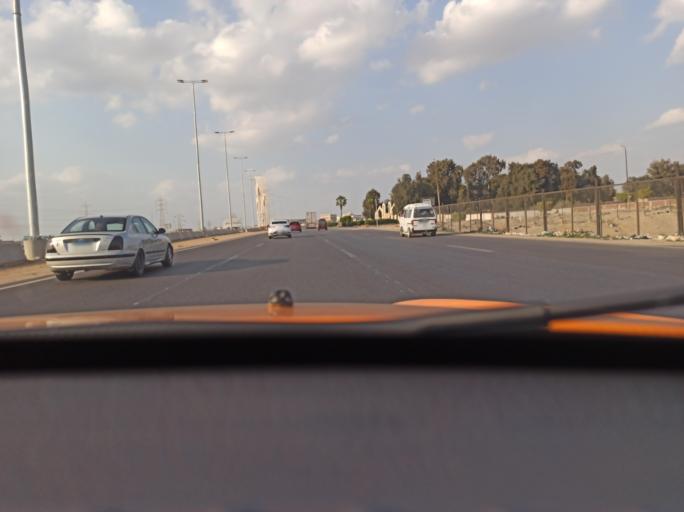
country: EG
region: Al Isma'iliyah
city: Ismailia
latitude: 30.5906
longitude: 32.1997
